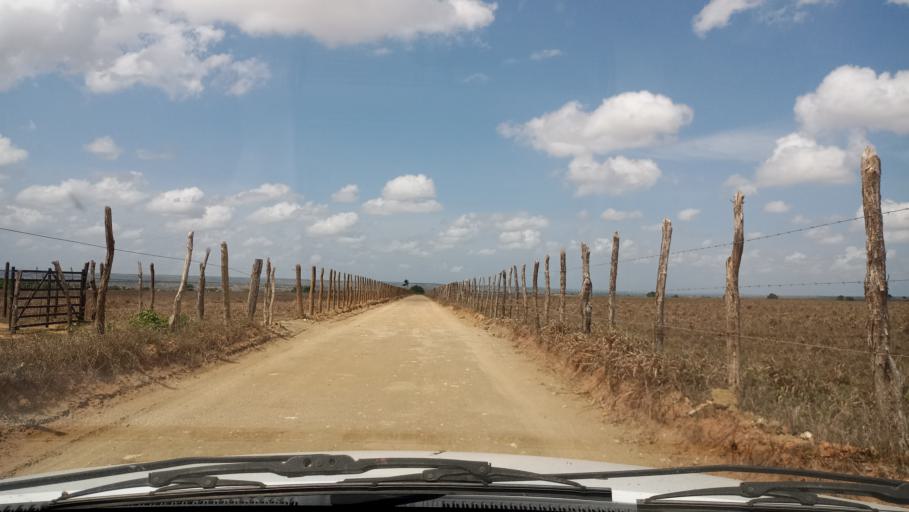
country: BR
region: Rio Grande do Norte
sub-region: Pedro Velho
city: Pedro Velho
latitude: -6.3509
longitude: -35.3328
